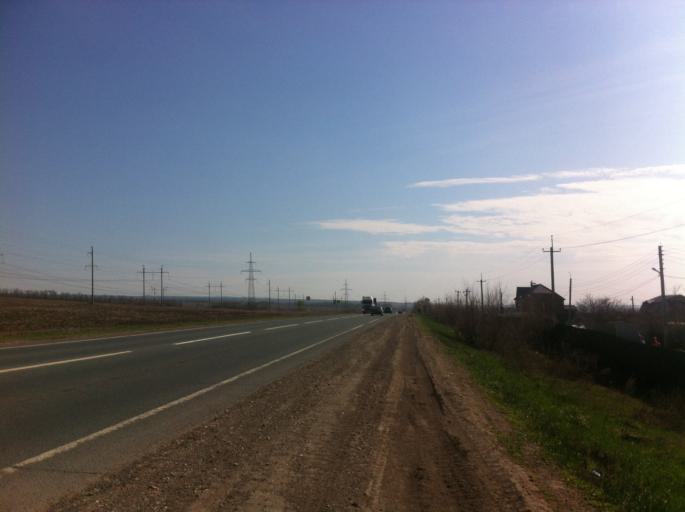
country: RU
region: Samara
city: Smyshlyayevka
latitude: 53.1168
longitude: 50.4150
